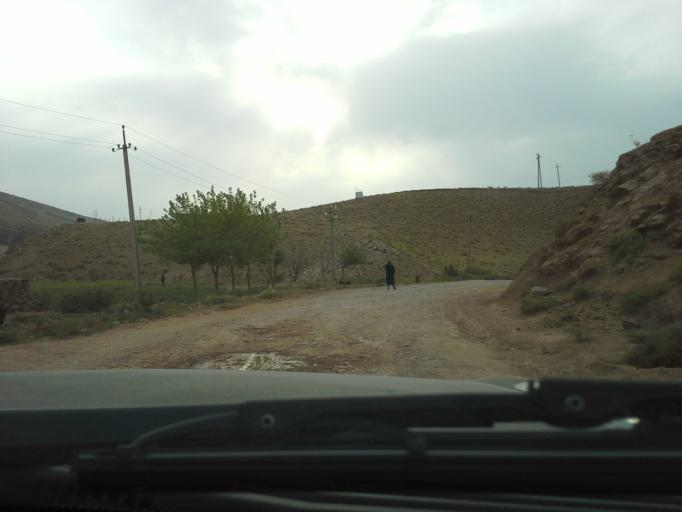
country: UZ
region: Qashqadaryo
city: Qorashina
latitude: 37.9381
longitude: 66.5277
